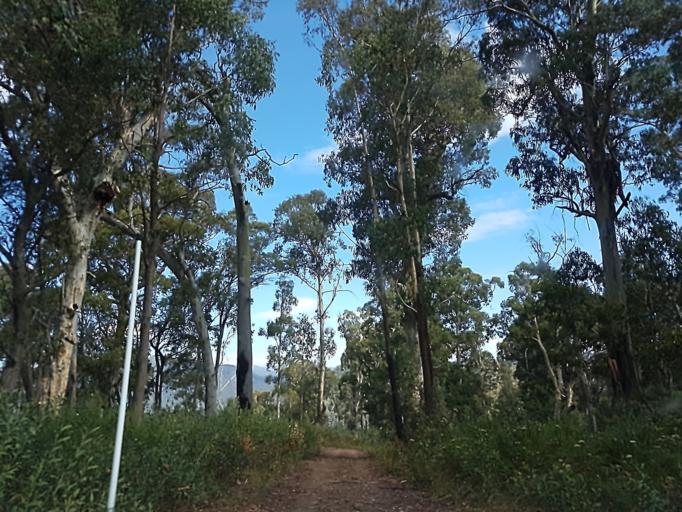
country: AU
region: Victoria
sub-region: Alpine
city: Mount Beauty
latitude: -36.9189
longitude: 146.9974
